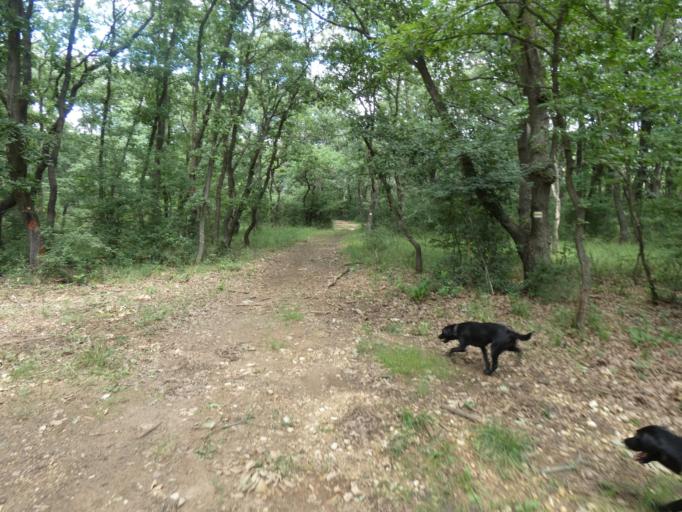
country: HU
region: Fejer
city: Csakvar
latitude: 47.4079
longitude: 18.3810
